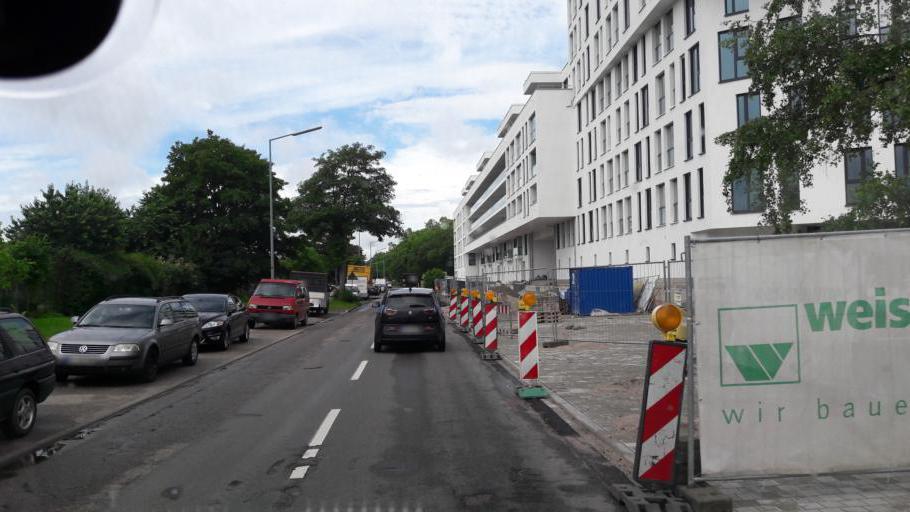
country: DE
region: Baden-Wuerttemberg
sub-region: Karlsruhe Region
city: Karlsruhe
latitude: 49.0000
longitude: 8.4197
